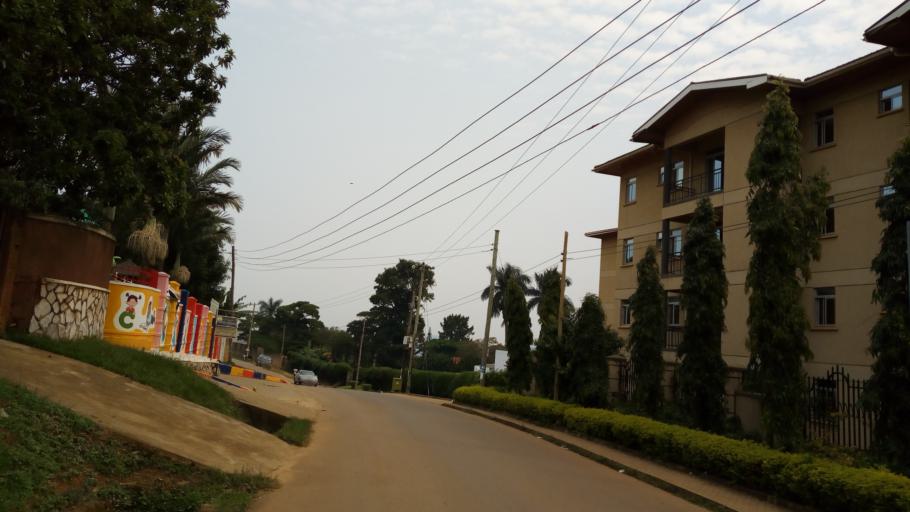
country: UG
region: Central Region
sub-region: Wakiso District
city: Kireka
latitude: 0.3164
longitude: 32.6397
